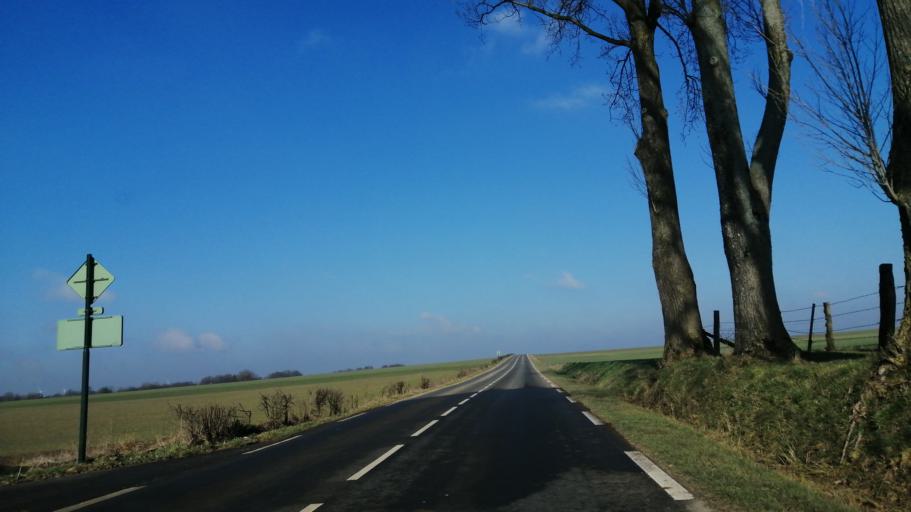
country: FR
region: Nord-Pas-de-Calais
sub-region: Departement du Pas-de-Calais
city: Maisnil-les-Ruitz
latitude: 50.4024
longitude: 2.6013
